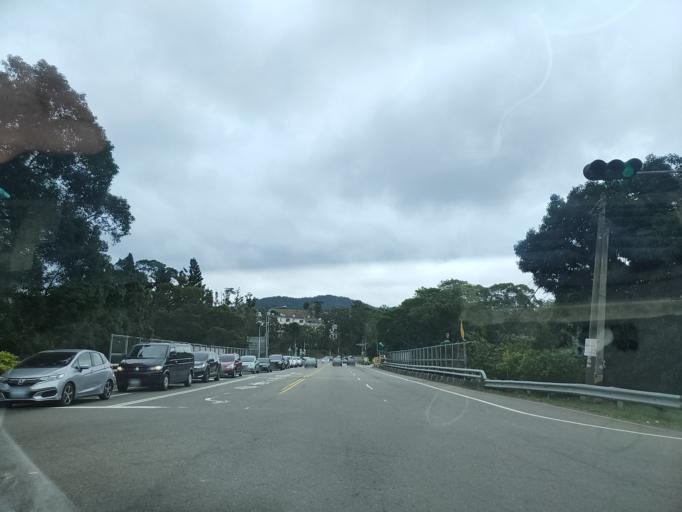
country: TW
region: Taiwan
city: Fengyuan
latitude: 24.3930
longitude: 120.7577
